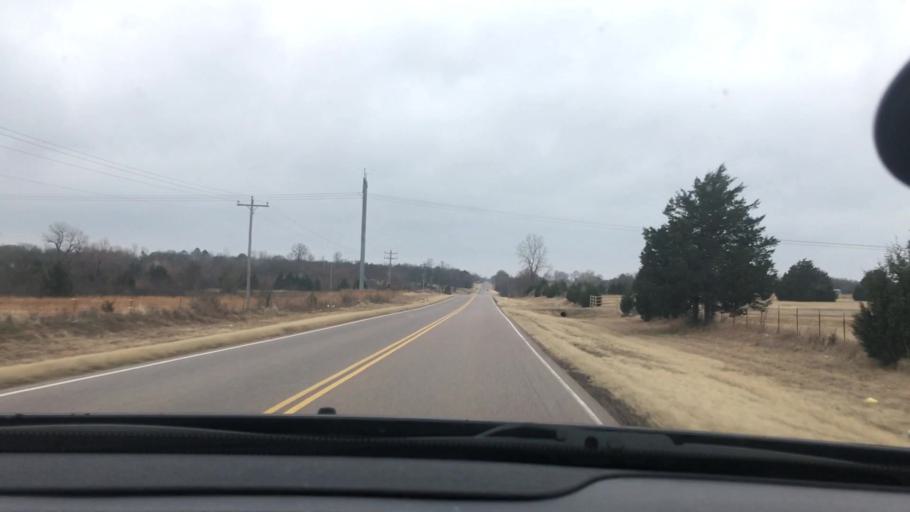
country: US
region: Oklahoma
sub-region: Johnston County
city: Tishomingo
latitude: 34.2689
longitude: -96.6711
